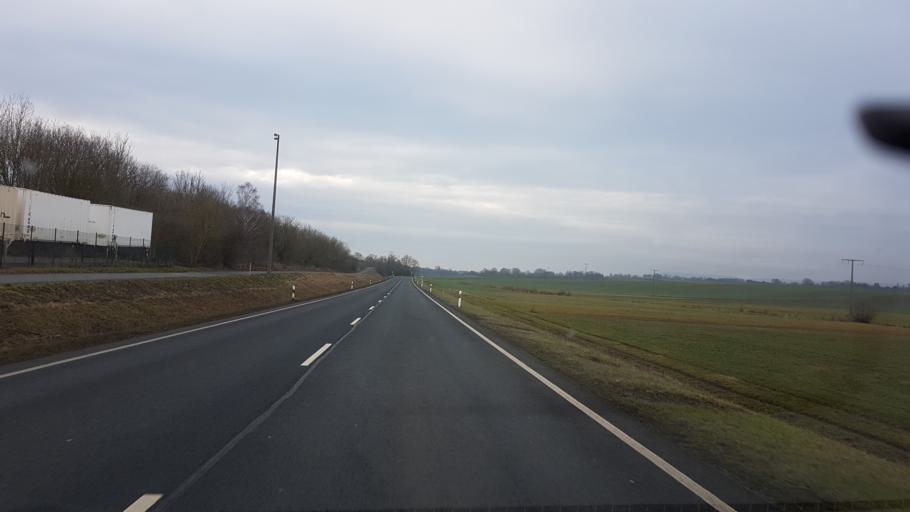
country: DE
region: Bavaria
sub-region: Regierungsbezirk Unterfranken
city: Ermershausen
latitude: 50.2363
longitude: 10.5687
